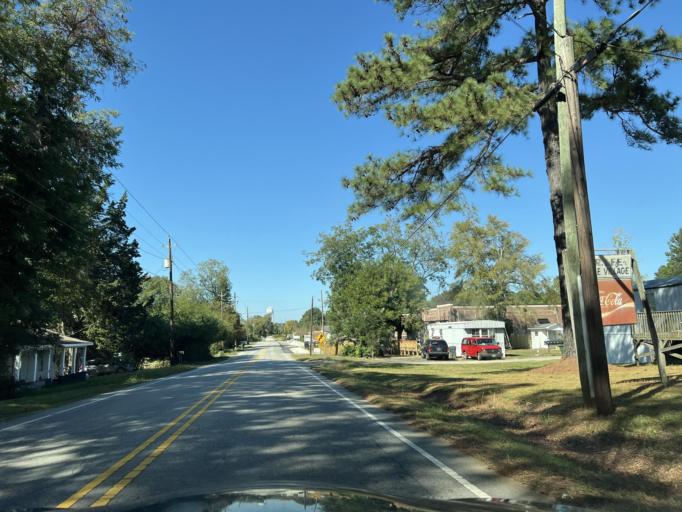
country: US
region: North Carolina
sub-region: Johnston County
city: Clayton
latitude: 35.6611
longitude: -78.4696
